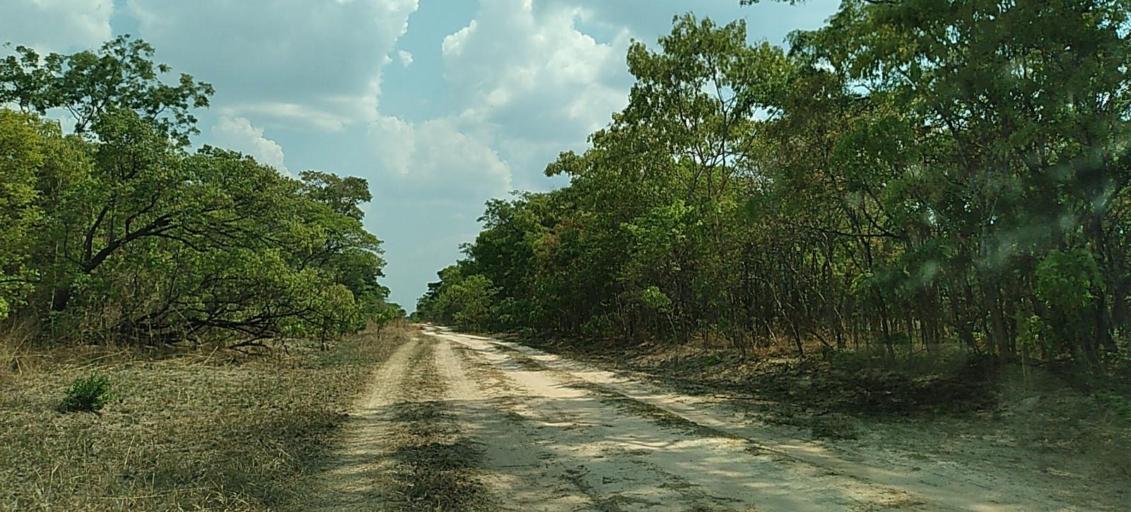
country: ZM
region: Copperbelt
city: Mpongwe
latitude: -13.8244
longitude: 27.9425
